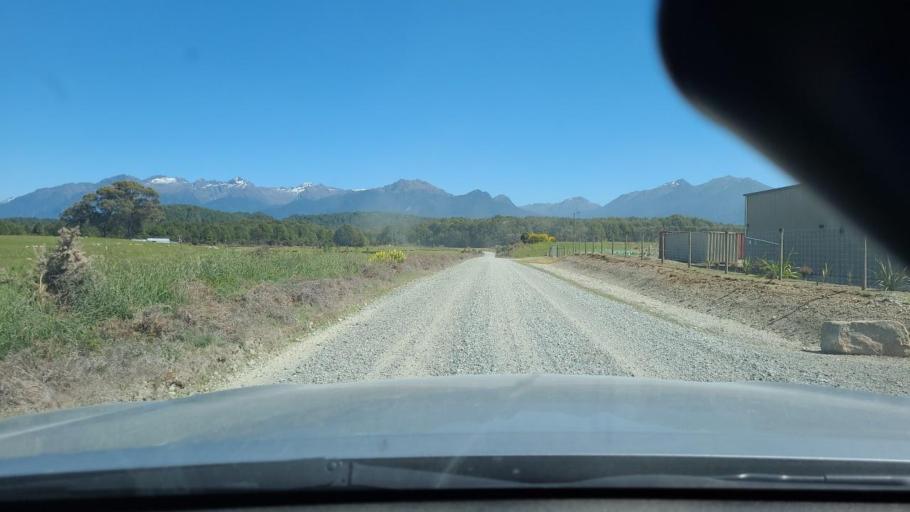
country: NZ
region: Southland
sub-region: Southland District
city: Te Anau
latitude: -45.5338
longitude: 167.6298
